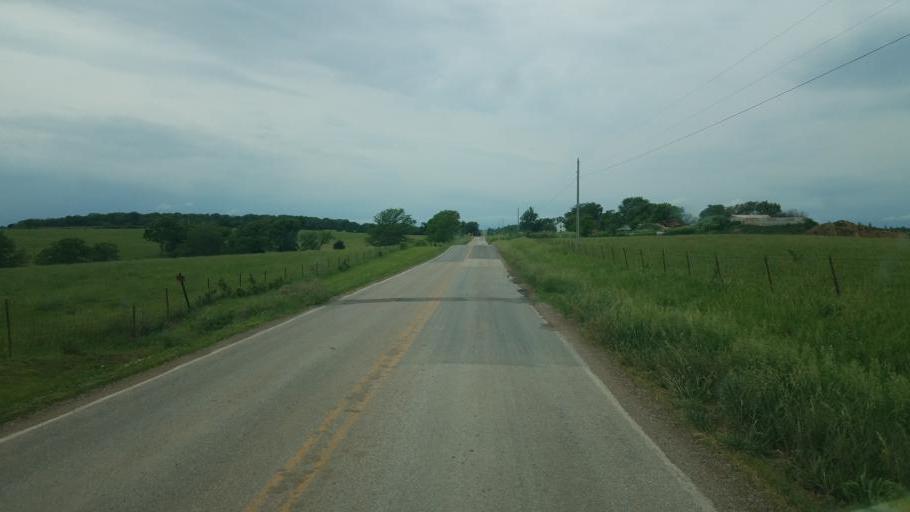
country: US
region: Missouri
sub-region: Moniteau County
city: California
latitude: 38.6955
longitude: -92.6283
